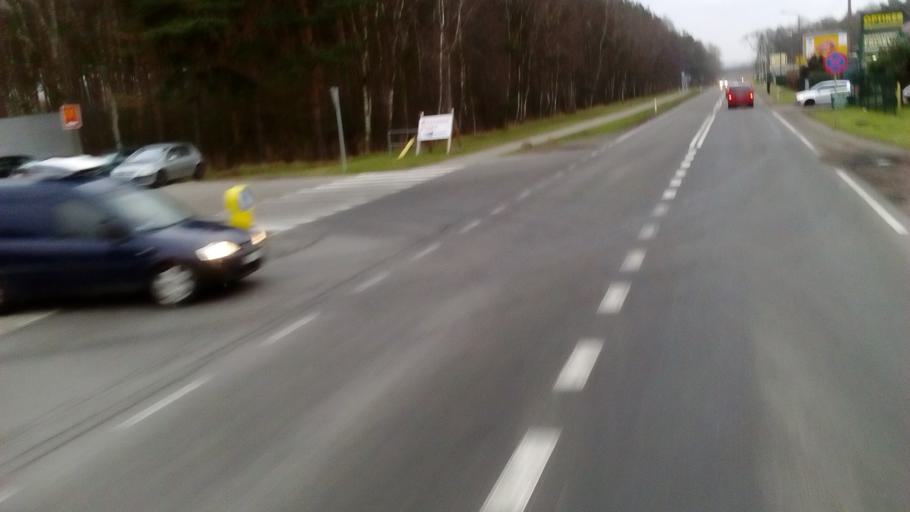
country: PL
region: West Pomeranian Voivodeship
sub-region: Powiat policki
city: Dobra
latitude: 53.4480
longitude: 14.3935
